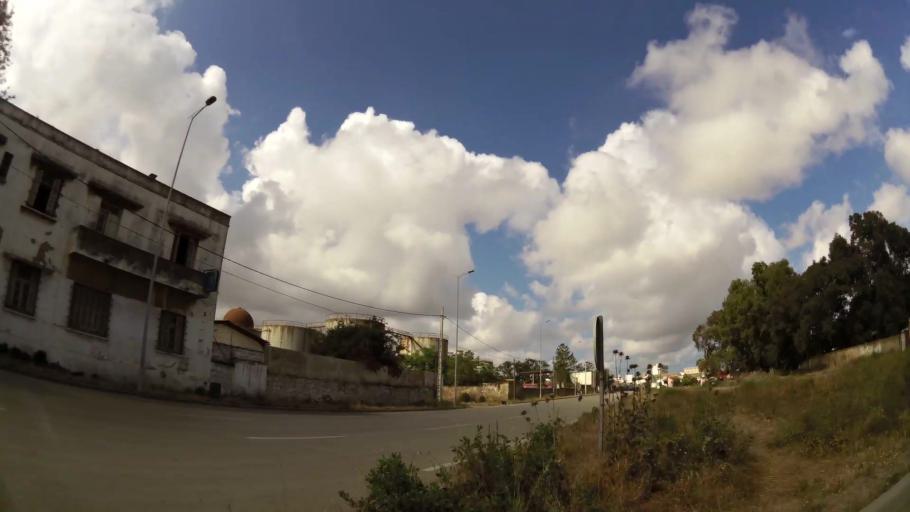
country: MA
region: Gharb-Chrarda-Beni Hssen
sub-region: Kenitra Province
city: Kenitra
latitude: 34.2688
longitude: -6.5680
